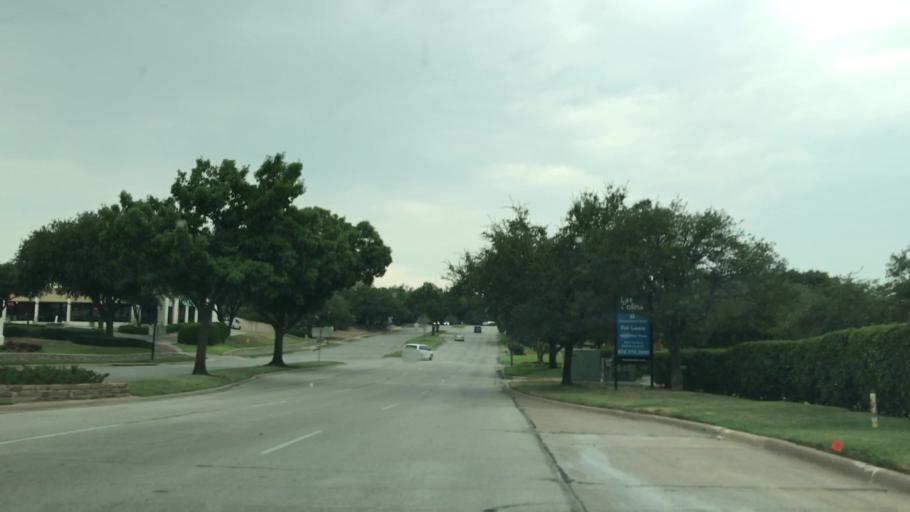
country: US
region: Texas
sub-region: Dallas County
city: Irving
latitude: 32.8851
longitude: -96.9646
